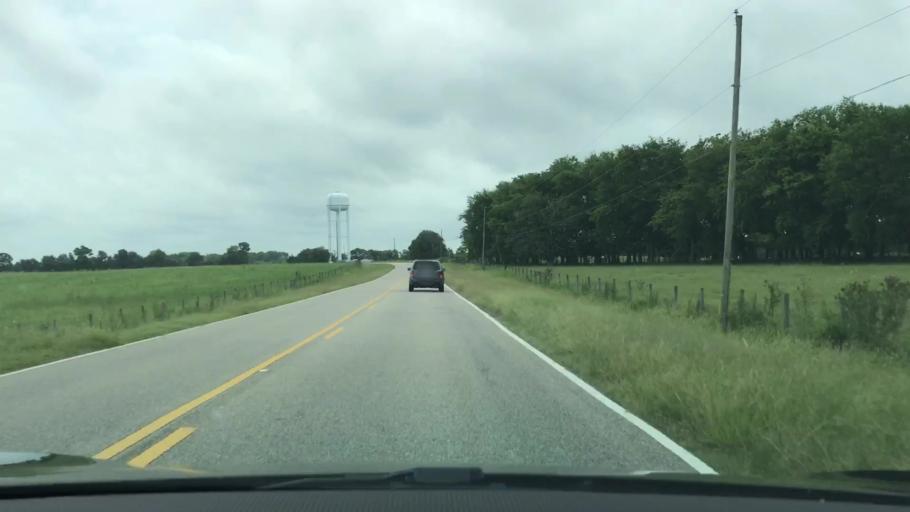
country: US
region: Alabama
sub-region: Montgomery County
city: Pike Road
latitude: 32.2833
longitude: -86.0923
